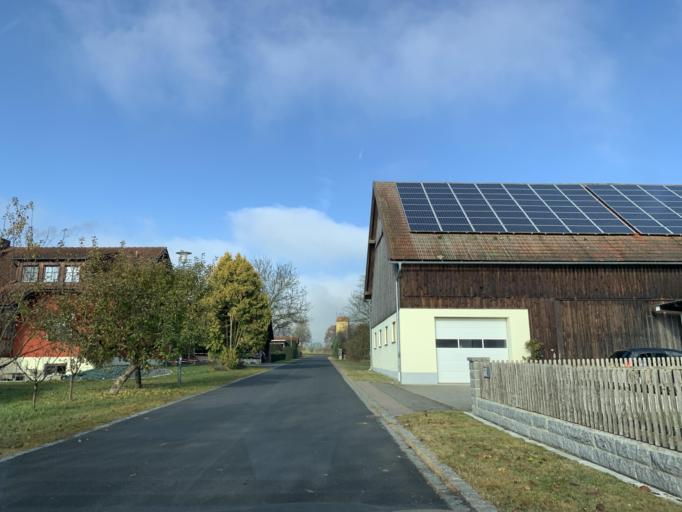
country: DE
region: Bavaria
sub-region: Upper Palatinate
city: Thanstein
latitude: 49.3943
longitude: 12.4739
